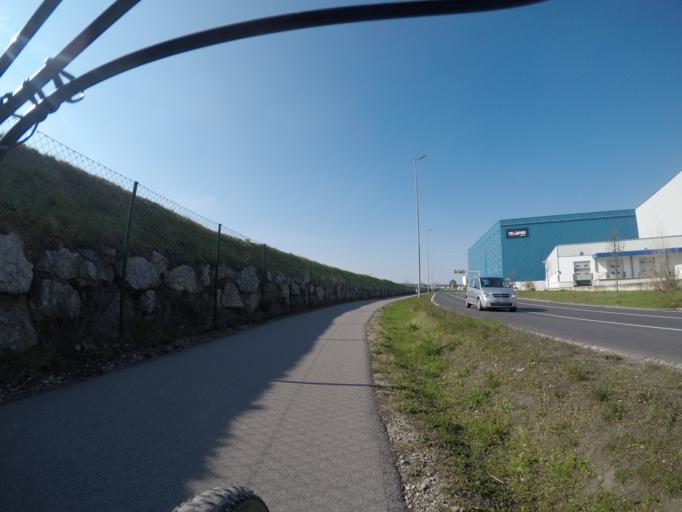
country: AT
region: Lower Austria
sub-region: Politischer Bezirk Modling
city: Neu-Guntramsdorf
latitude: 48.0599
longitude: 16.3364
